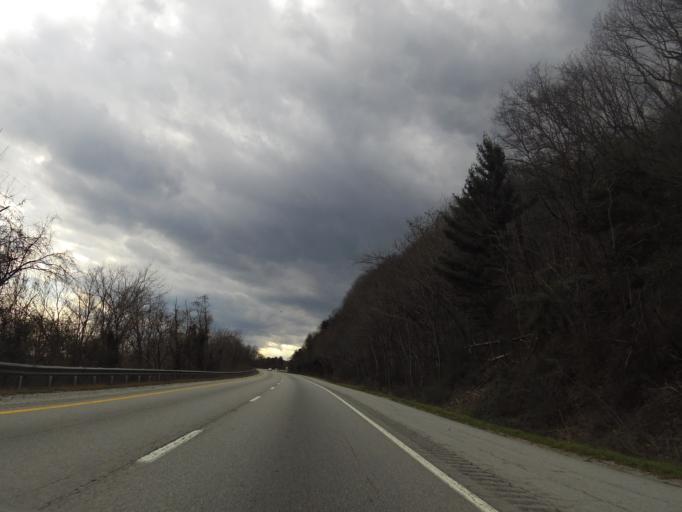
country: US
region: Tennessee
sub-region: Roane County
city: Rockwood
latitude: 35.8936
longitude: -84.6721
